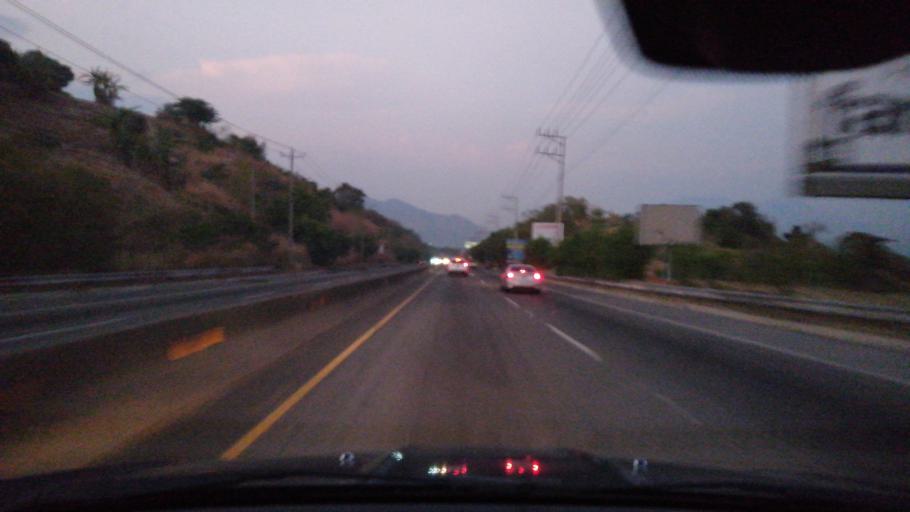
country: SV
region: San Salvador
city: Mejicanos
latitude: 13.7490
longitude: -89.2180
